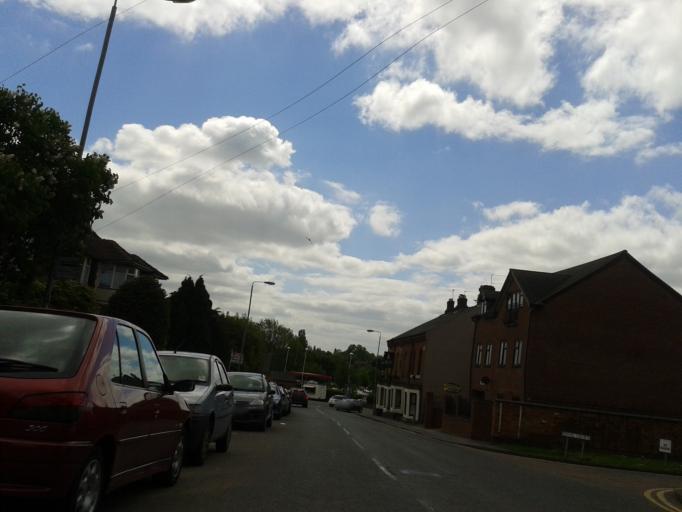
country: GB
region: England
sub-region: Leicestershire
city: Hinckley
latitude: 52.5369
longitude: -1.3724
